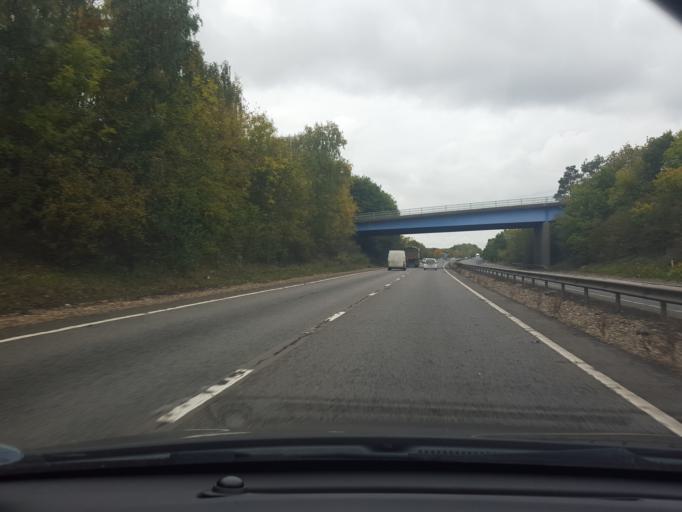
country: GB
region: England
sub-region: Suffolk
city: Needham Market
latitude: 52.1613
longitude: 1.0599
